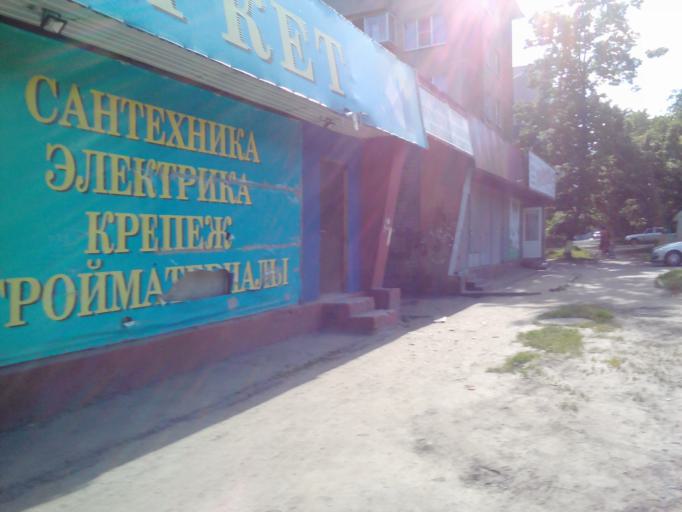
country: RU
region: Kursk
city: Voroshnevo
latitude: 51.6676
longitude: 36.0889
